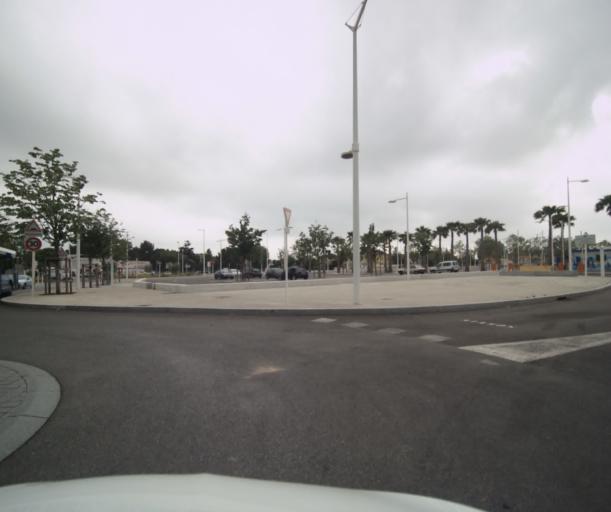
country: FR
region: Provence-Alpes-Cote d'Azur
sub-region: Departement du Var
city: La Seyne-sur-Mer
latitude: 43.1290
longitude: 5.8815
